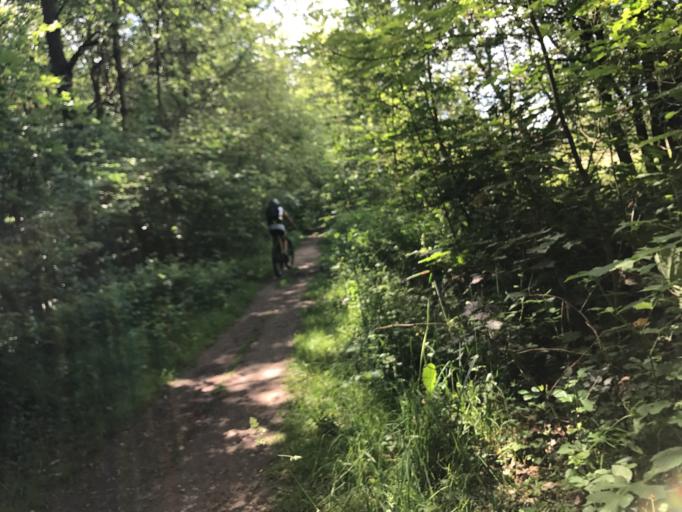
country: DE
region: Hesse
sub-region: Regierungsbezirk Darmstadt
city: Schlangenbad
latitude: 50.0837
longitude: 8.1242
